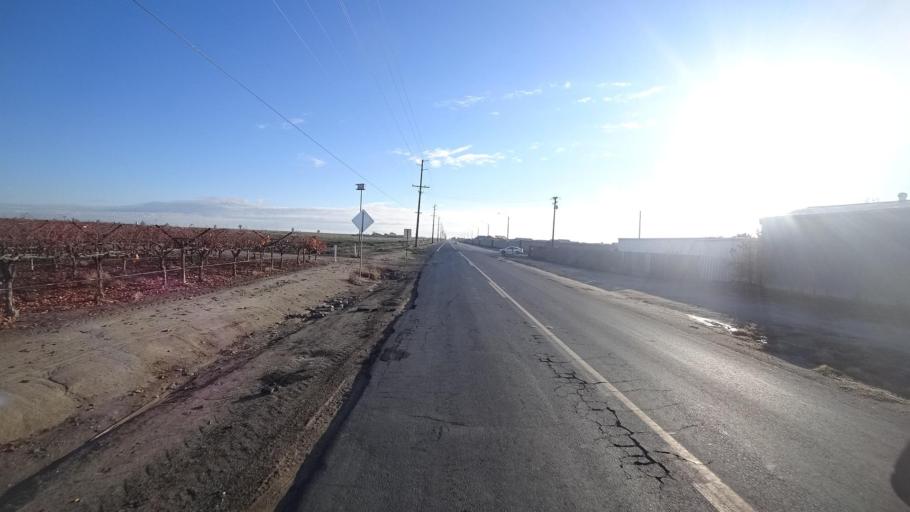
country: US
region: California
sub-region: Kern County
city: Delano
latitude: 35.7904
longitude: -119.2771
